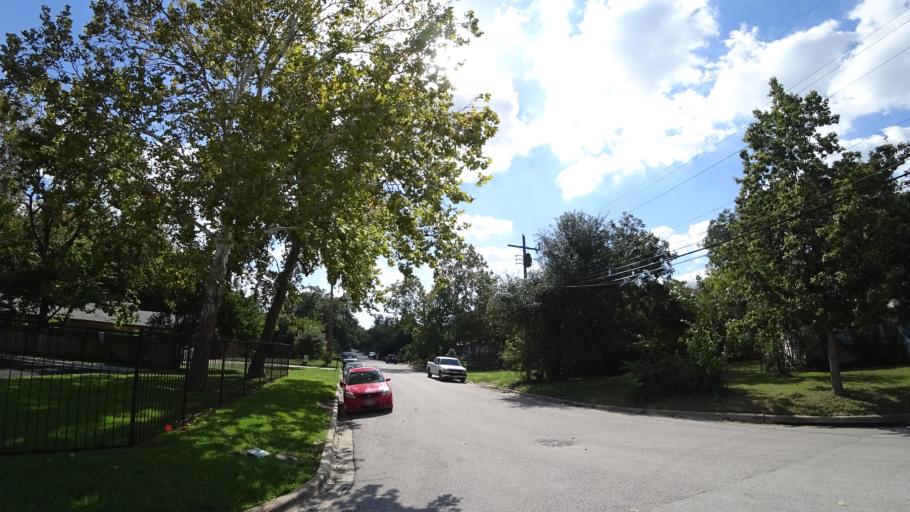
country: US
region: Texas
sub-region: Travis County
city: Austin
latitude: 30.3145
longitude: -97.7093
